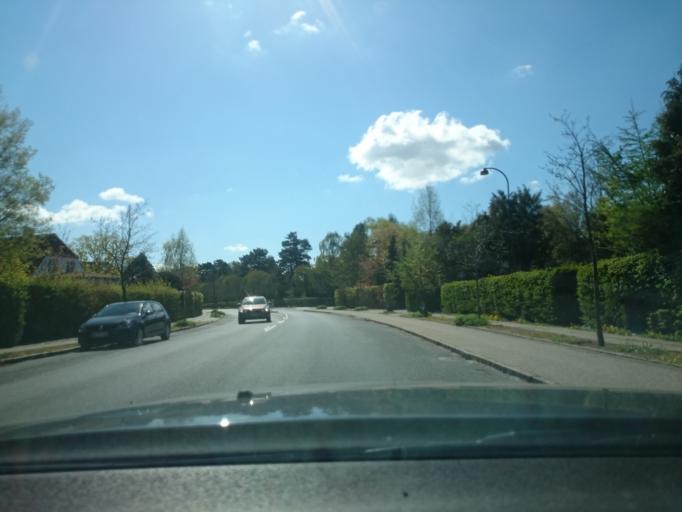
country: DK
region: Capital Region
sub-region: Gentofte Kommune
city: Charlottenlund
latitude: 55.7669
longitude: 12.5776
